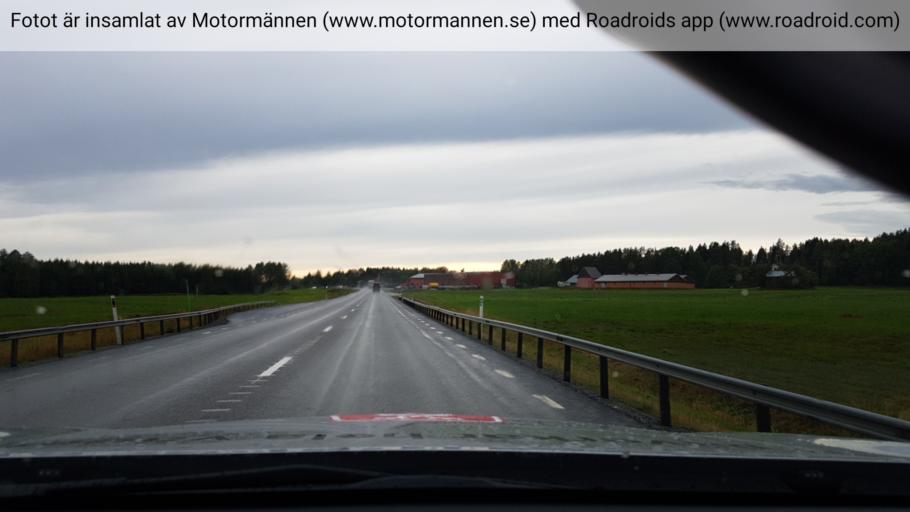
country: SE
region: Vaesterbotten
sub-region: Robertsfors Kommun
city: Robertsfors
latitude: 64.2368
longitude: 21.0243
